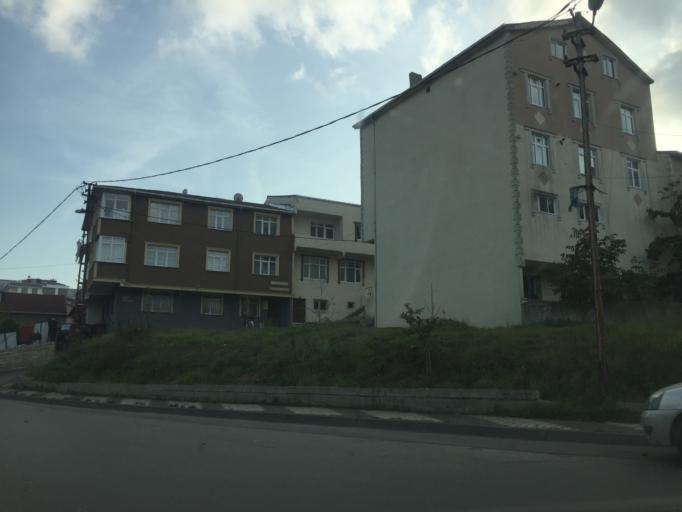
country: TR
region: Istanbul
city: Sultanbeyli
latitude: 40.9436
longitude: 29.2982
